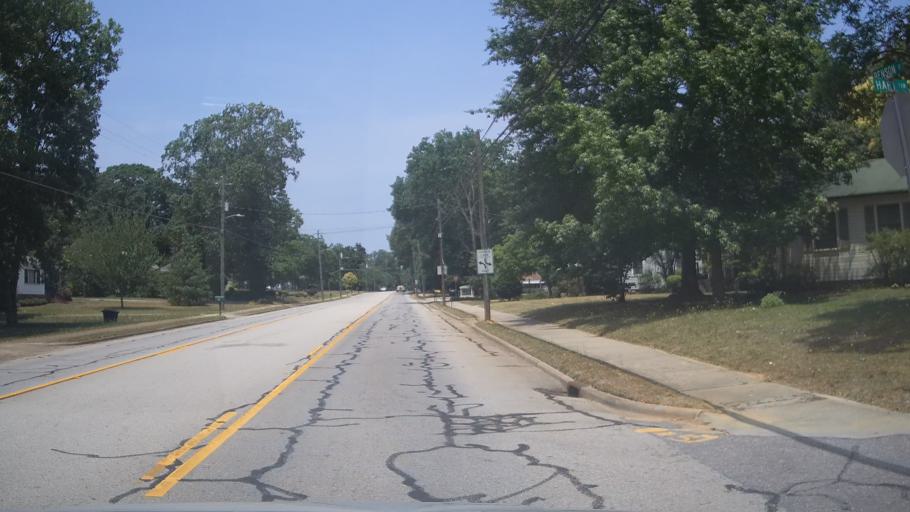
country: US
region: Georgia
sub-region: Hart County
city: Hartwell
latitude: 34.3430
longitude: -82.9240
